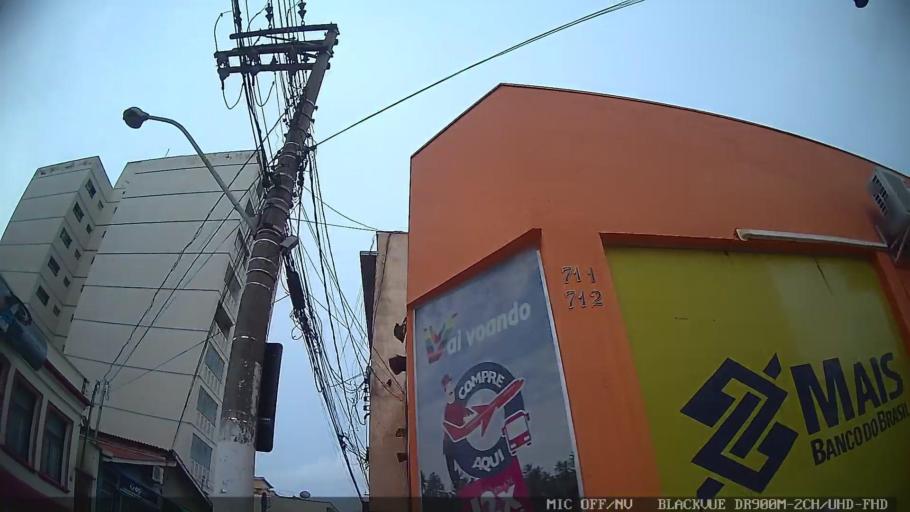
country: BR
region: Sao Paulo
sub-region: Braganca Paulista
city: Braganca Paulista
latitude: -22.9578
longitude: -46.5411
